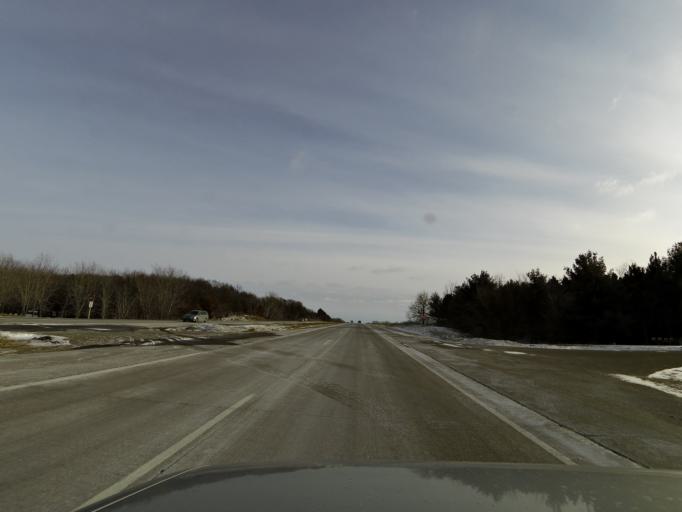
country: US
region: Minnesota
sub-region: Washington County
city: Lake Saint Croix Beach
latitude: 44.9281
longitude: -92.6812
